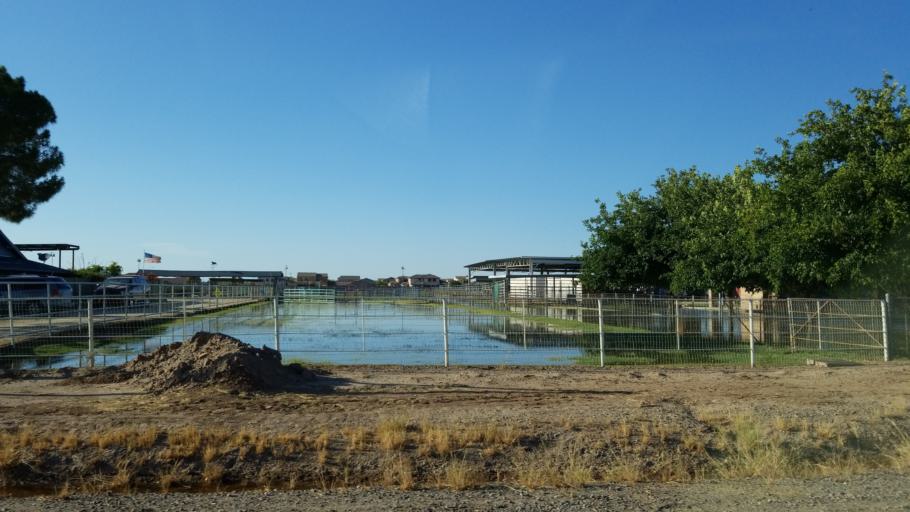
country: US
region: Arizona
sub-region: Maricopa County
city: Laveen
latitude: 33.3774
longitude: -112.2101
